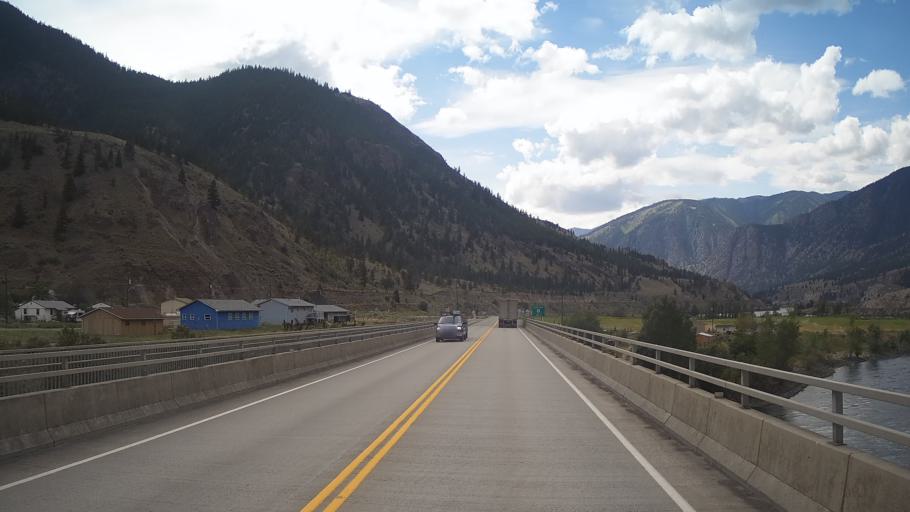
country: CA
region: British Columbia
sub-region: Thompson-Nicola Regional District
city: Ashcroft
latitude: 50.4180
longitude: -121.3551
